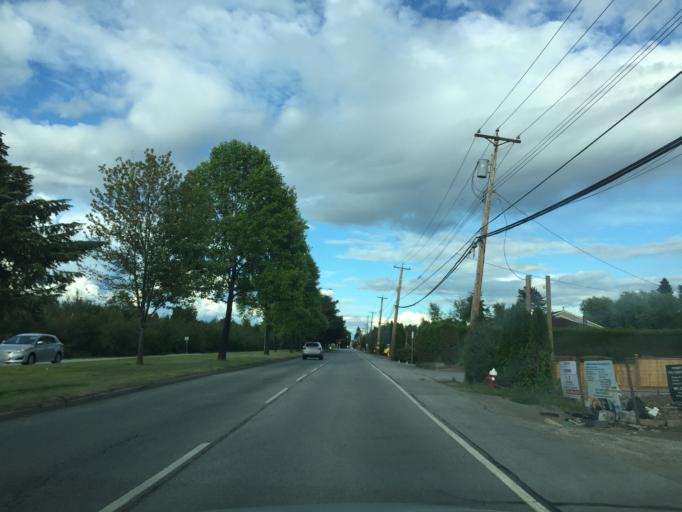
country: CA
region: British Columbia
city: Richmond
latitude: 49.1700
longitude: -123.1081
